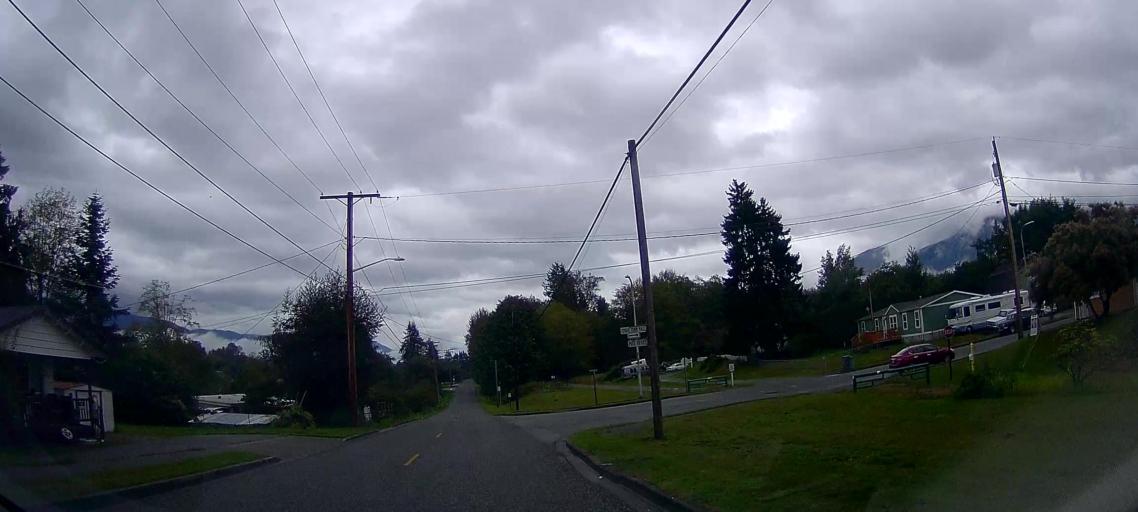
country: US
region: Washington
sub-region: Skagit County
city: Sedro-Woolley
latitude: 48.5266
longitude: -122.0603
